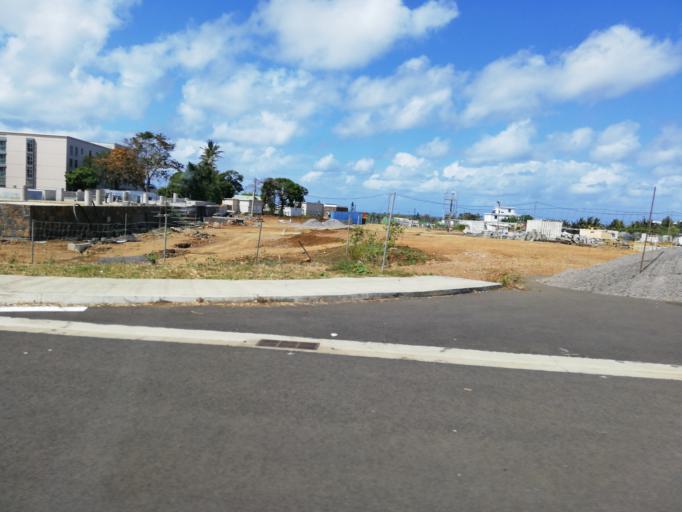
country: MU
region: Grand Port
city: Plaine Magnien
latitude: -20.4404
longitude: 57.6696
